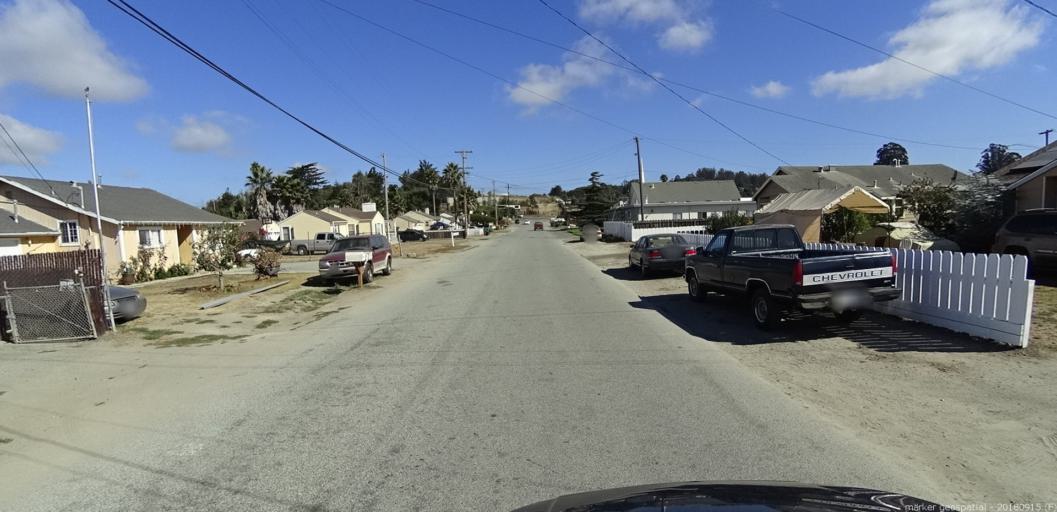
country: US
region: California
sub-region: Monterey County
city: Las Lomas
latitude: 36.8636
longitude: -121.7352
